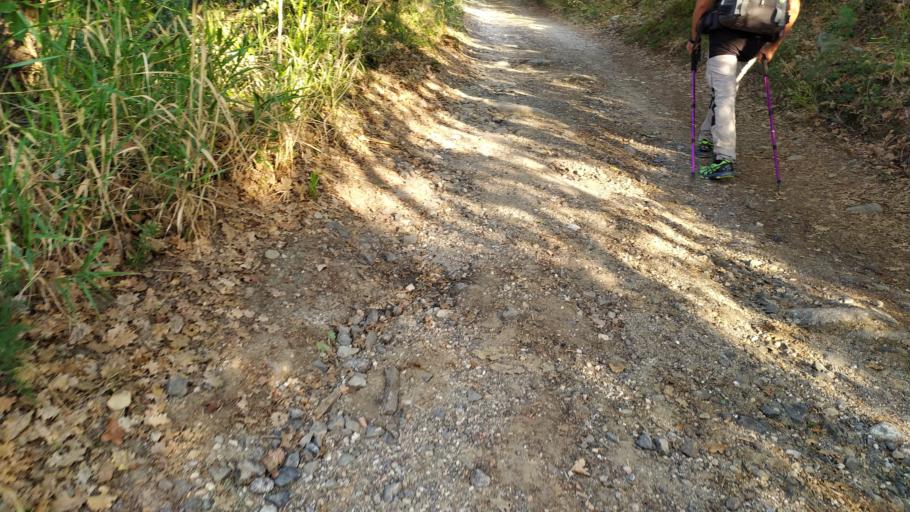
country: IT
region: Sicily
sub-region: Messina
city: Saponara Marittima
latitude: 38.2258
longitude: 15.4287
